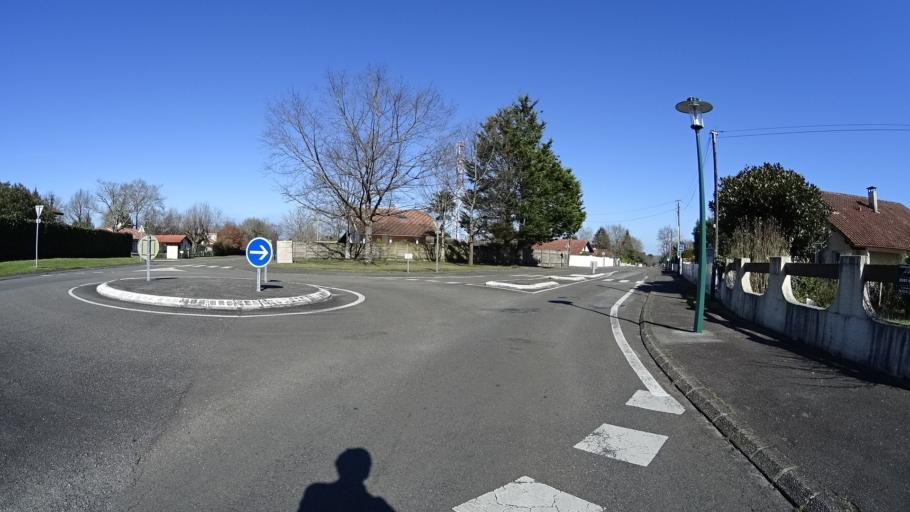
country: FR
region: Aquitaine
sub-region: Departement des Landes
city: Saint-Paul-les-Dax
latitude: 43.7324
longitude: -1.0854
